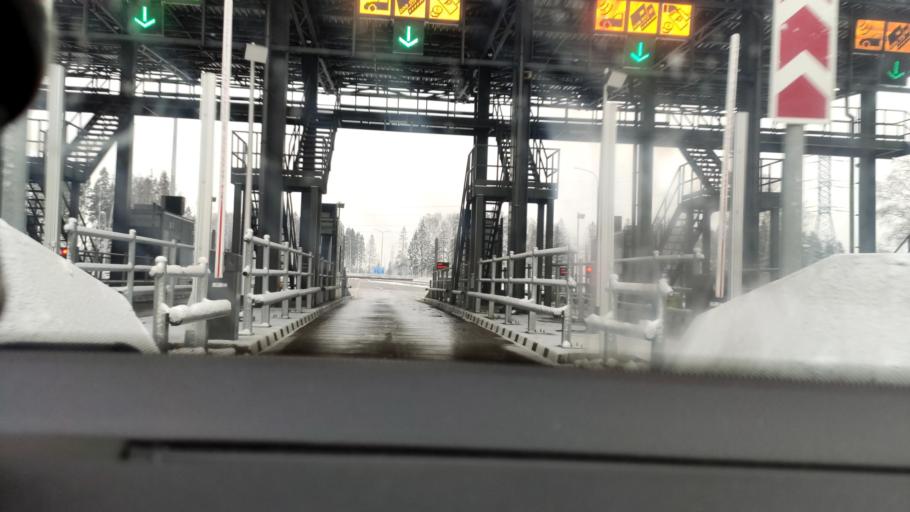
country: RU
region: Moskovskaya
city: Solnechnogorsk
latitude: 56.1611
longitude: 36.9149
